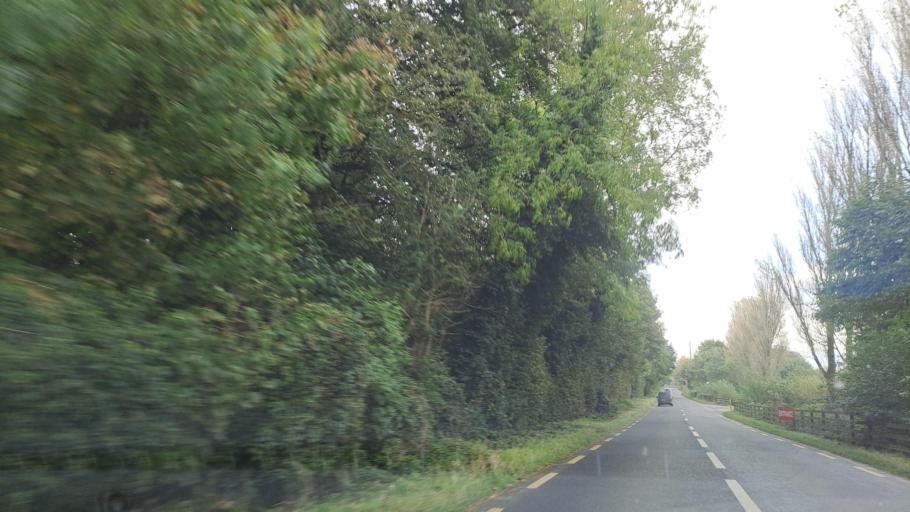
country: IE
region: Ulster
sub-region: An Cabhan
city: Kingscourt
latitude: 53.8644
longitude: -6.7930
